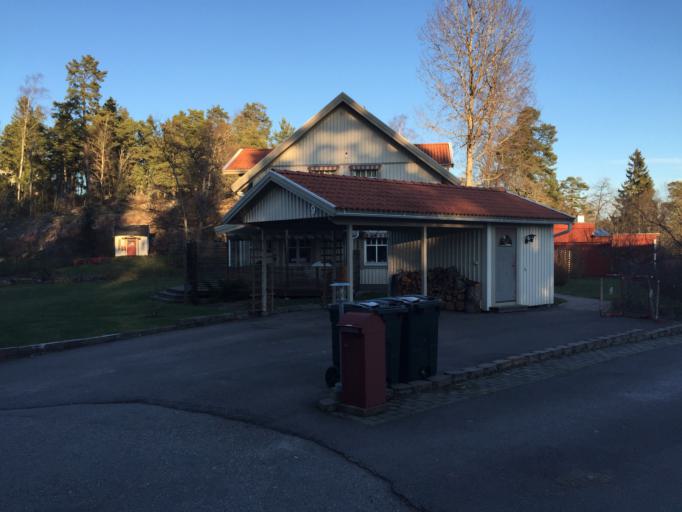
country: SE
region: Stockholm
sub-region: Salems Kommun
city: Ronninge
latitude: 59.1873
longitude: 17.7618
